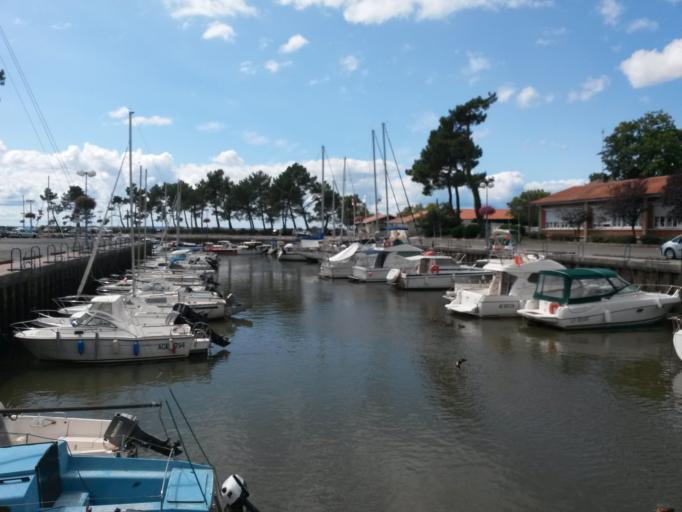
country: FR
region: Aquitaine
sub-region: Departement de la Gironde
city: Andernos-les-Bains
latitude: 44.7360
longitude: -1.0928
